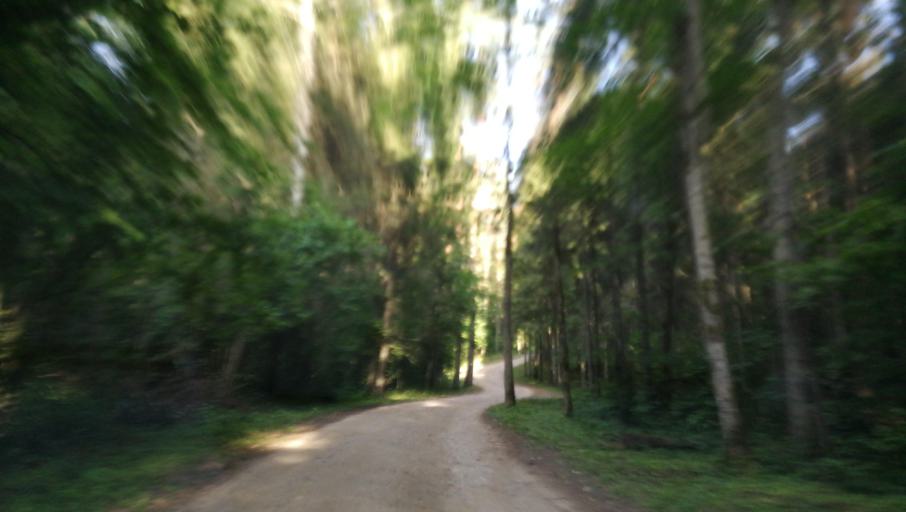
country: LV
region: Cesu Rajons
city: Cesis
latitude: 57.2861
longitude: 25.2126
